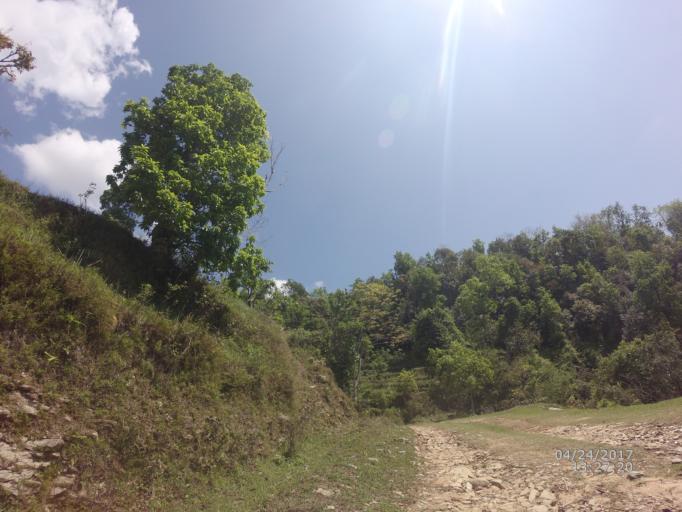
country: NP
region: Western Region
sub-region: Gandaki Zone
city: Pokhara
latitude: 28.1902
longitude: 84.1045
